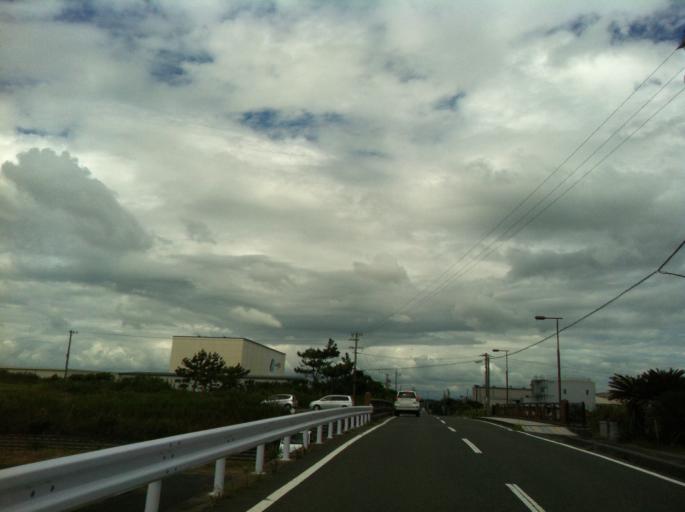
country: JP
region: Shizuoka
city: Kakegawa
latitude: 34.6492
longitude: 138.0658
